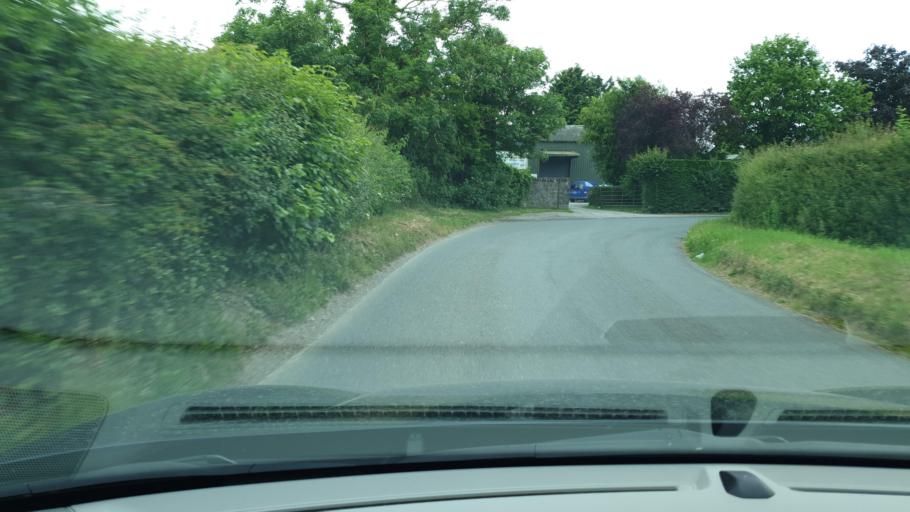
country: IE
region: Leinster
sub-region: An Mhi
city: Ashbourne
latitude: 53.4612
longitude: -6.3811
